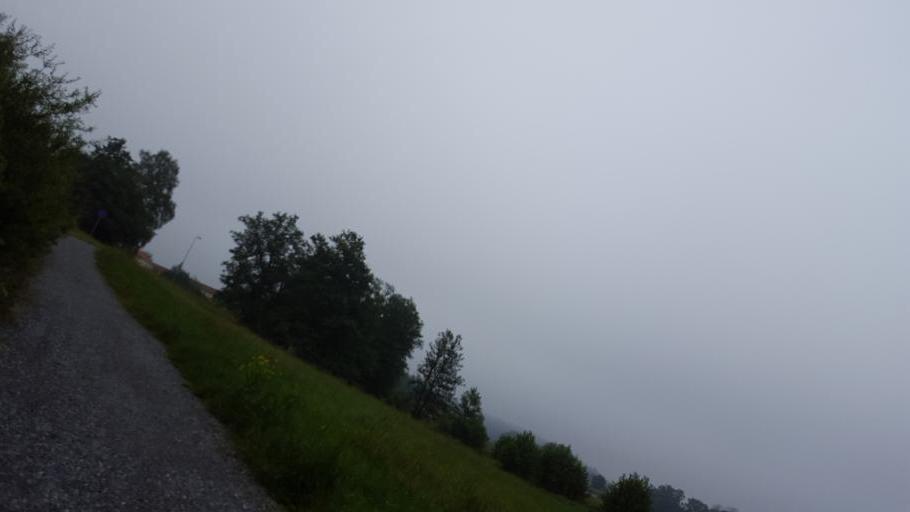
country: SE
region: Stockholm
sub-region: Upplands Vasby Kommun
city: Upplands Vaesby
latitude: 59.5090
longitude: 17.8817
